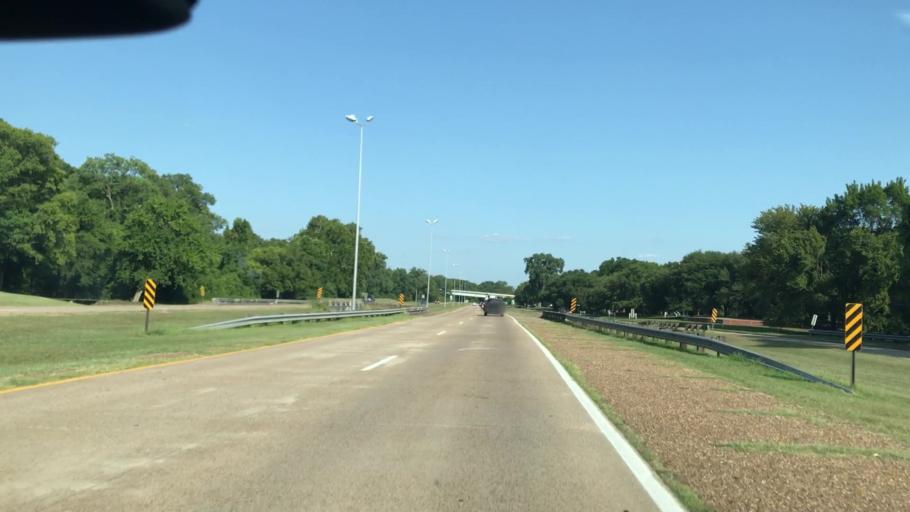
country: US
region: Louisiana
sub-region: Bossier Parish
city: Bossier City
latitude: 32.4952
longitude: -93.7090
